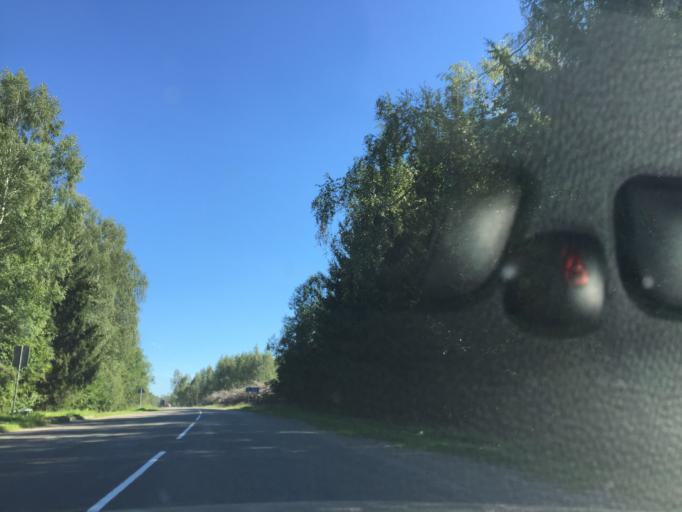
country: LV
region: Akniste
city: Akniste
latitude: 56.1136
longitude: 25.8384
